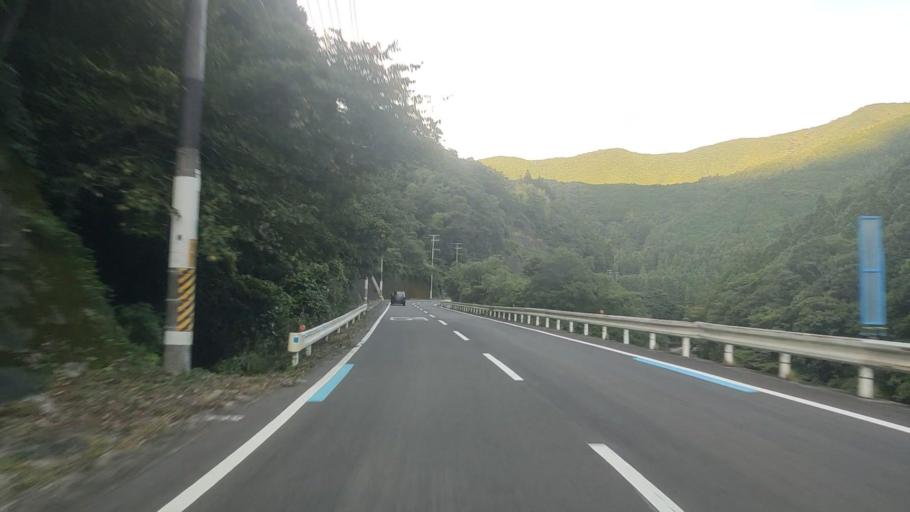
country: JP
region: Wakayama
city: Tanabe
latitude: 33.8110
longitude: 135.5456
